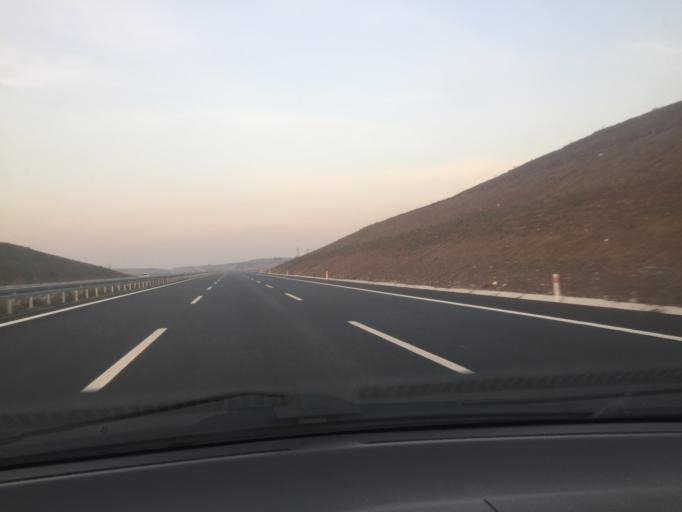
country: TR
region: Bursa
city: Mahmudiye
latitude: 40.2669
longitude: 28.6405
